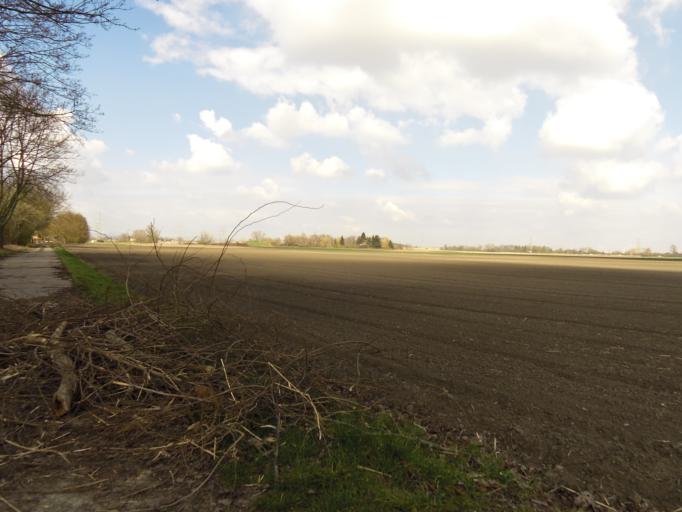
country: DE
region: Rheinland-Pfalz
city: Lambsheim
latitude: 49.5180
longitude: 8.3068
